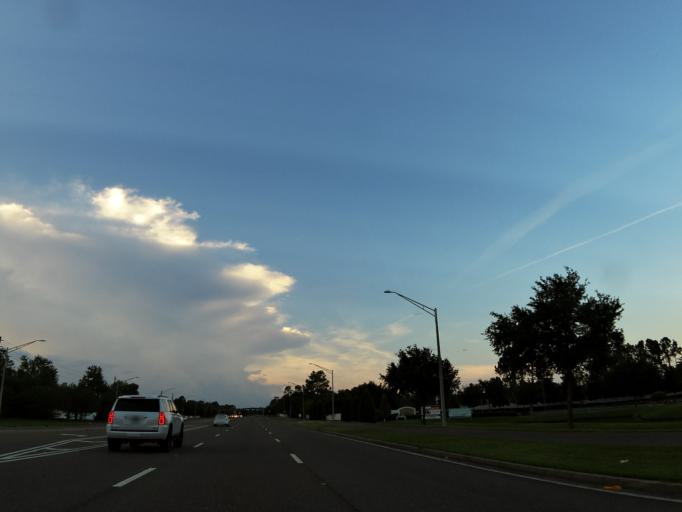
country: US
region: Florida
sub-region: Duval County
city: Jacksonville Beach
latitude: 30.2672
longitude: -81.4952
